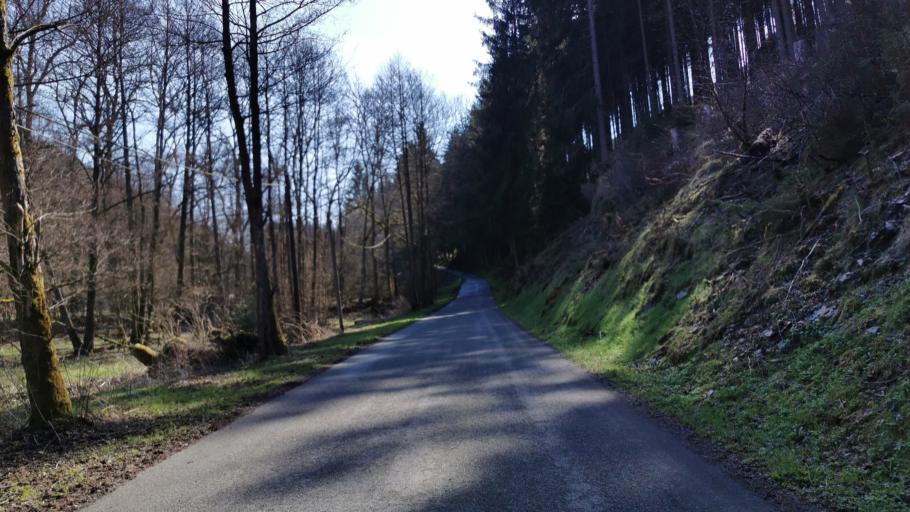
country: DE
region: Thuringia
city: Probstzella
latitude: 50.5159
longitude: 11.3998
